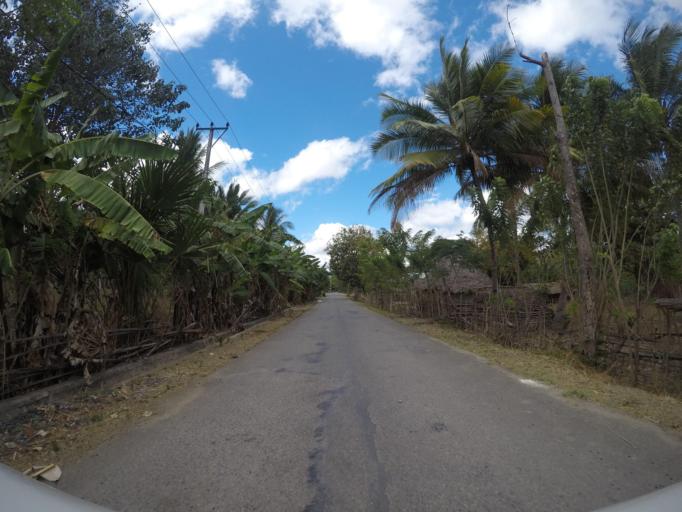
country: TL
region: Lautem
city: Lospalos
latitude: -8.4482
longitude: 126.8239
